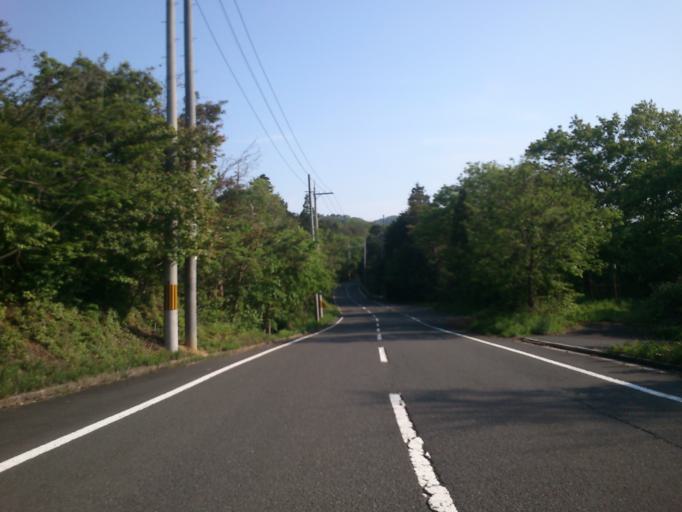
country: JP
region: Kyoto
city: Miyazu
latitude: 35.7442
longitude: 135.1737
